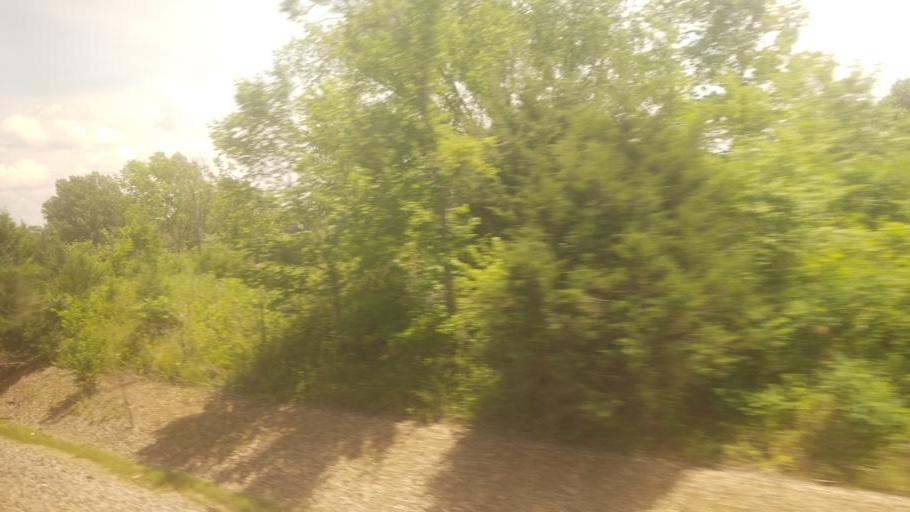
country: US
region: Missouri
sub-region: Macon County
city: La Plata
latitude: 40.0668
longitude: -92.4566
